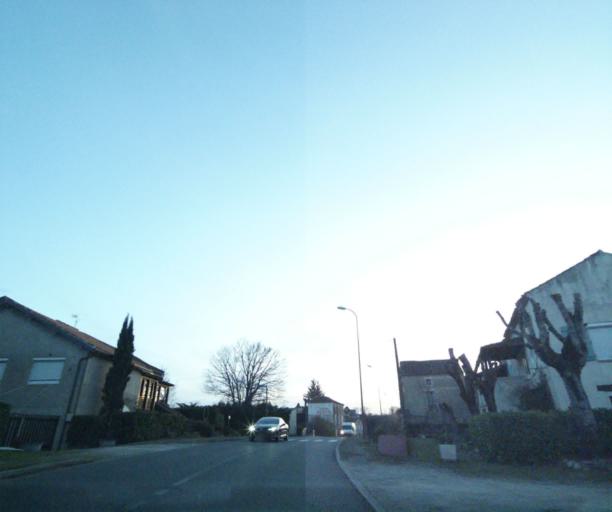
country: FR
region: Midi-Pyrenees
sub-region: Departement du Lot
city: Pradines
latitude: 44.5249
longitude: 1.4568
